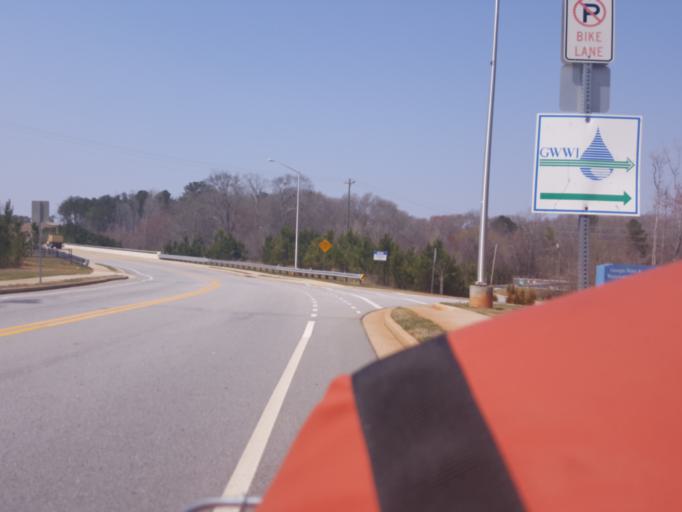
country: US
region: Georgia
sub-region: Carroll County
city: Carrollton
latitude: 33.5772
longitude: -85.1121
